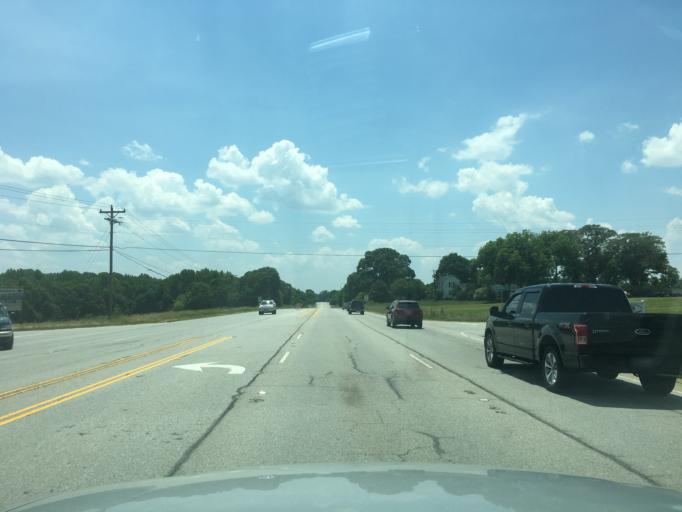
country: US
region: South Carolina
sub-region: Anderson County
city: Northlake
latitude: 34.6142
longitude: -82.6086
